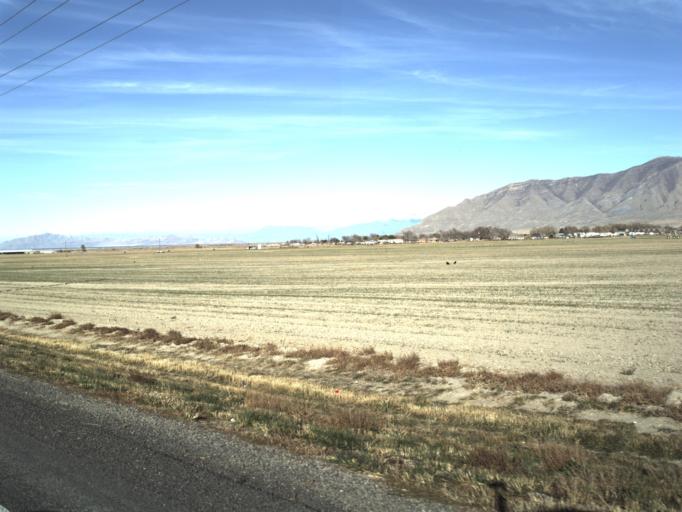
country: US
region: Utah
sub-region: Tooele County
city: Erda
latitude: 40.5951
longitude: -112.3704
